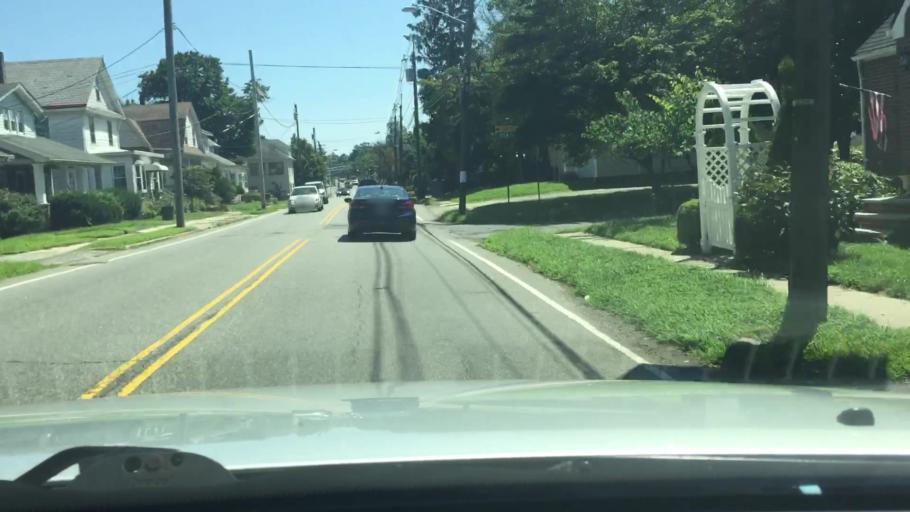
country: US
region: New Jersey
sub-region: Middlesex County
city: South River
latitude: 40.4433
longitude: -74.3924
